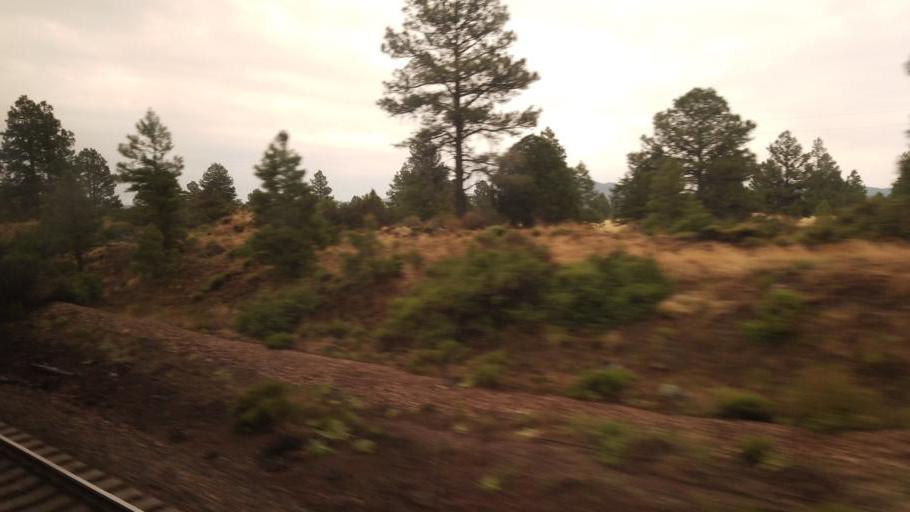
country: US
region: Arizona
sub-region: Coconino County
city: Parks
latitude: 35.2411
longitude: -111.9773
